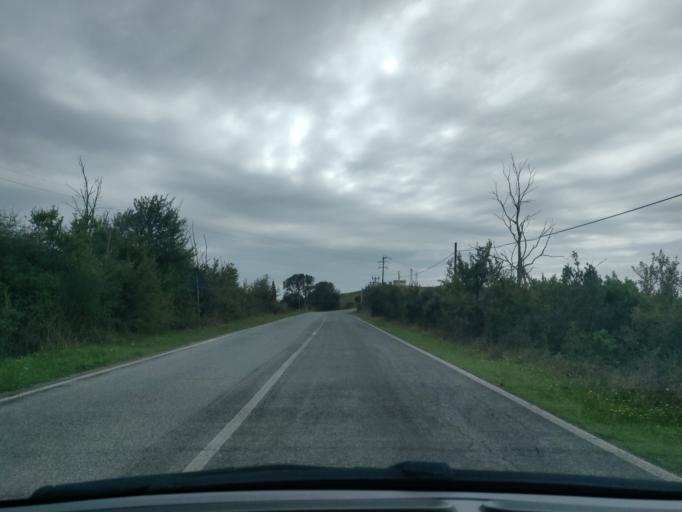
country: IT
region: Latium
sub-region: Citta metropolitana di Roma Capitale
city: Allumiere
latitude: 42.1189
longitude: 11.8615
